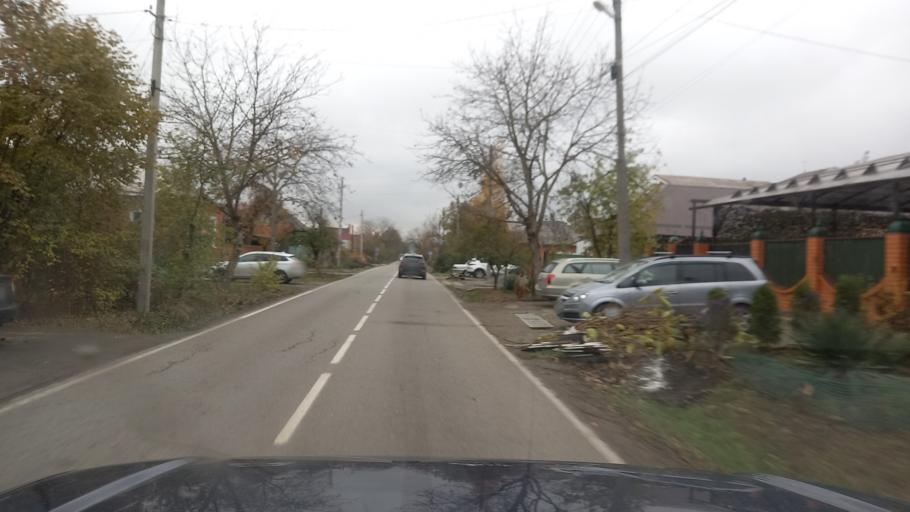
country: RU
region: Adygeya
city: Maykop
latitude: 44.6041
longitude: 40.0769
